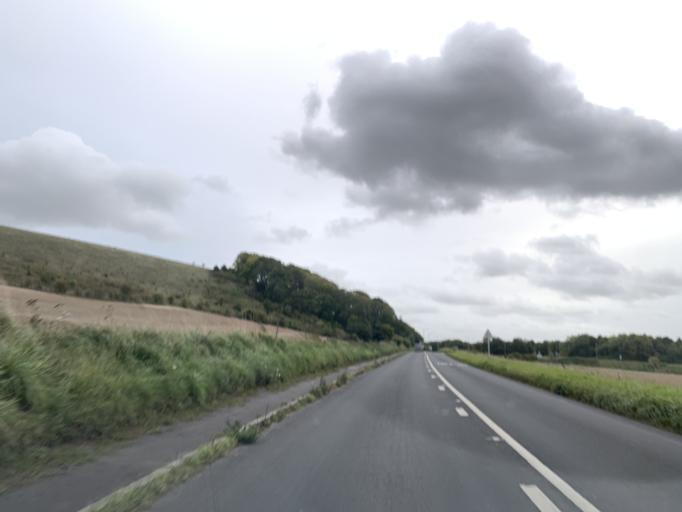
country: GB
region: England
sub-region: Wiltshire
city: Bishopstrow
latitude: 51.1879
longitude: -2.1227
